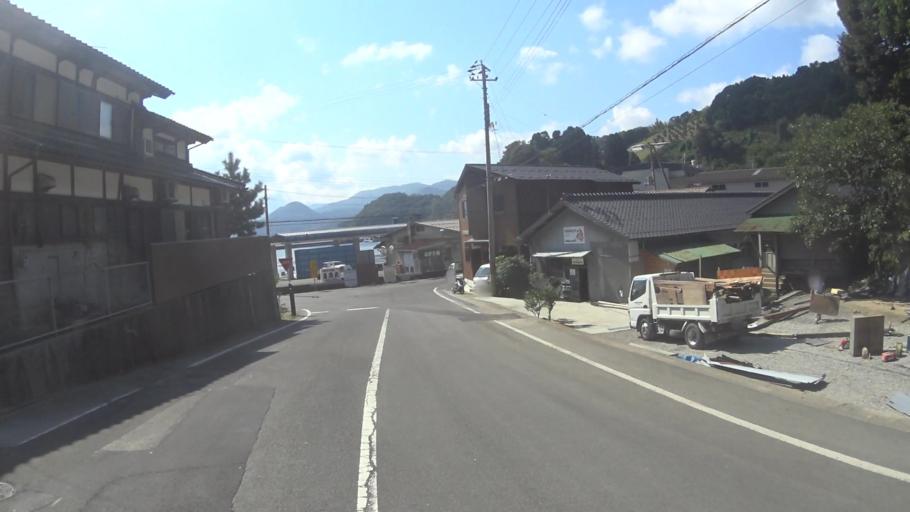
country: JP
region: Kyoto
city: Miyazu
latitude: 35.6749
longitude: 135.2950
